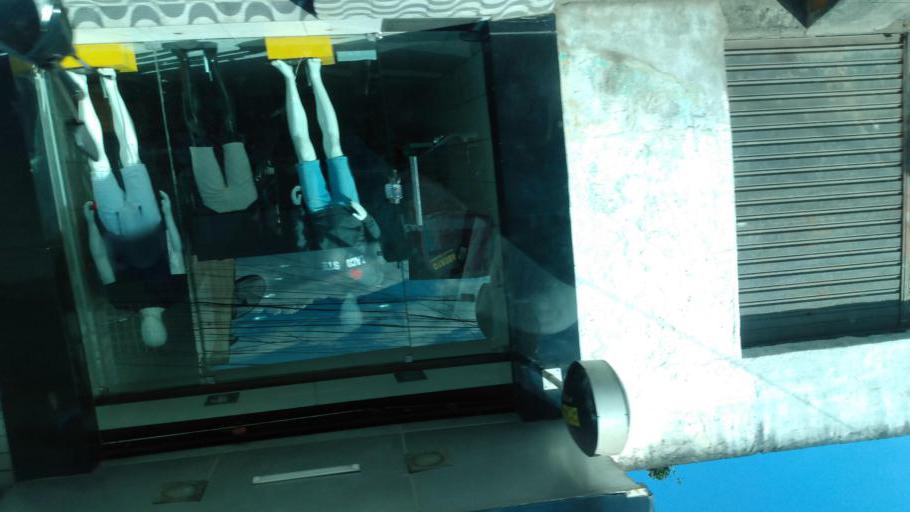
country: ET
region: Oromiya
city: Gore
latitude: 8.1997
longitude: 35.5719
